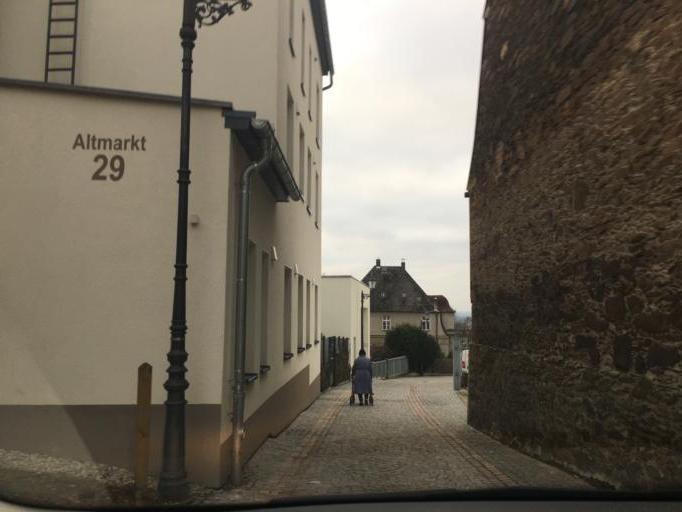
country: DE
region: Saxony
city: Hohenstein-Ernstthal
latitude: 50.8016
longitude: 12.7067
